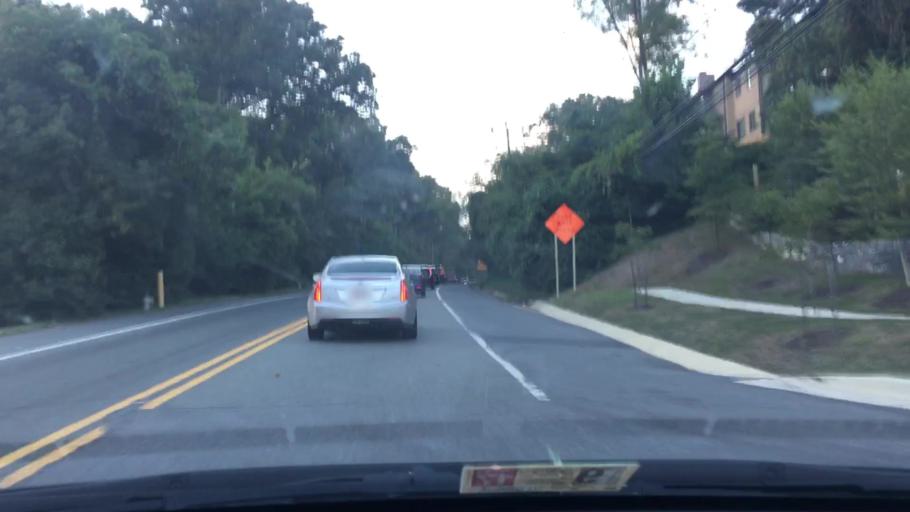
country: US
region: Maryland
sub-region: Montgomery County
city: North Bethesda
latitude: 39.0285
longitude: -77.1618
